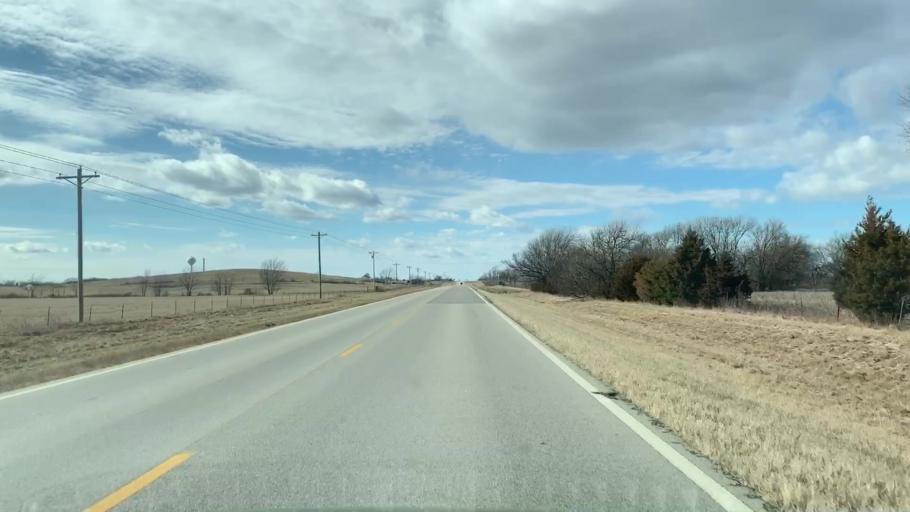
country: US
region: Kansas
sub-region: Neosho County
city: Erie
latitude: 37.5293
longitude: -95.3508
